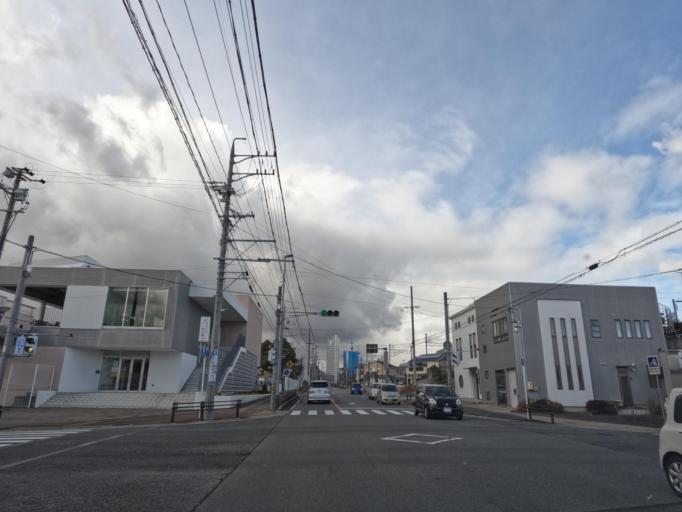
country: JP
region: Aichi
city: Chiryu
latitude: 34.9880
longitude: 137.0149
